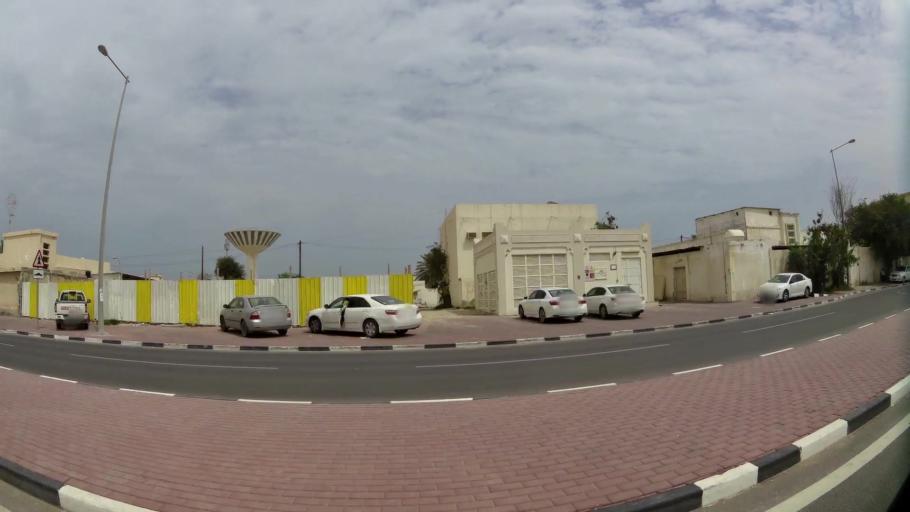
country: QA
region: Baladiyat ar Rayyan
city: Ar Rayyan
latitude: 25.3287
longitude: 51.4713
